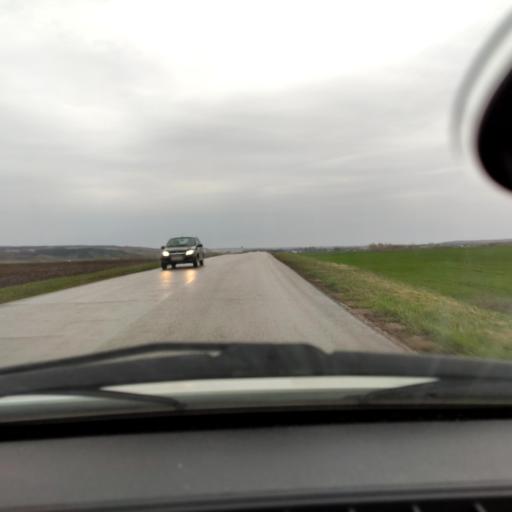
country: RU
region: Bashkortostan
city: Tolbazy
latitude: 54.1711
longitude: 55.9267
